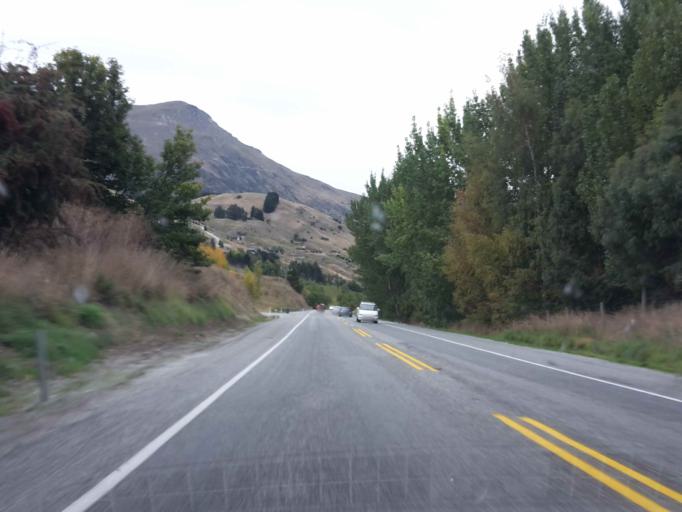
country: NZ
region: Otago
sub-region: Queenstown-Lakes District
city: Arrowtown
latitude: -44.9816
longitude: 168.8228
